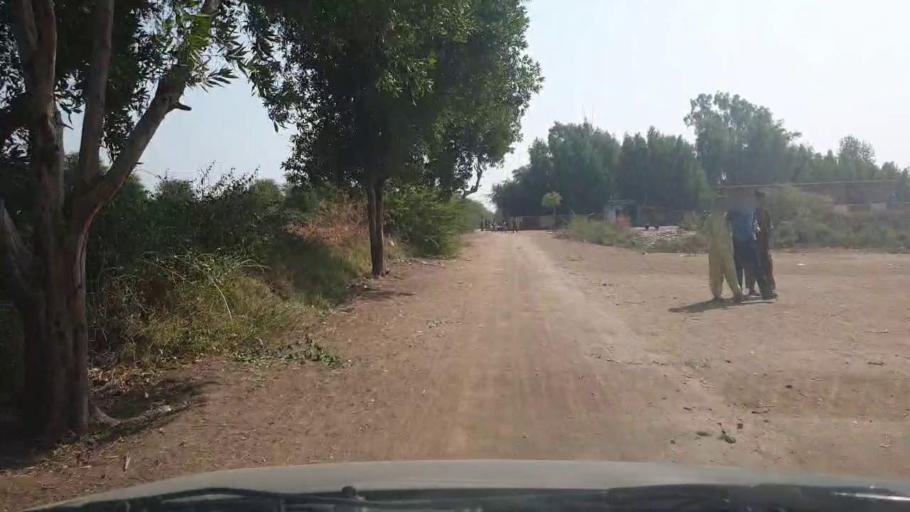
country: PK
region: Sindh
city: Mirwah Gorchani
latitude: 25.2759
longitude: 69.1363
